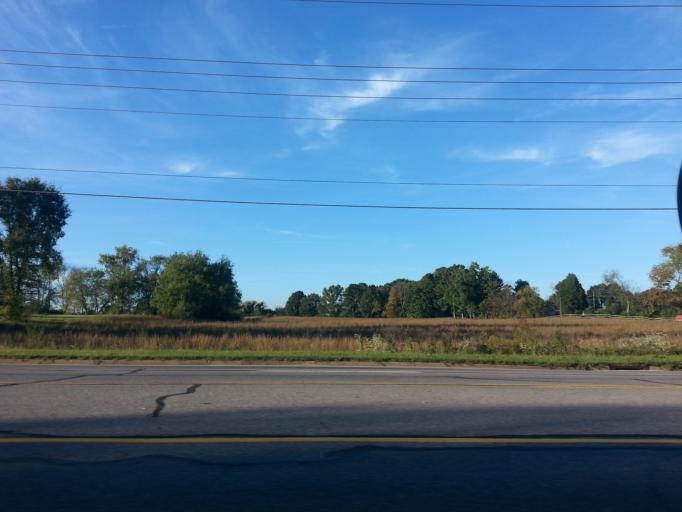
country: US
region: Tennessee
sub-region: Blount County
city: Eagleton Village
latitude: 35.7562
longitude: -83.9271
